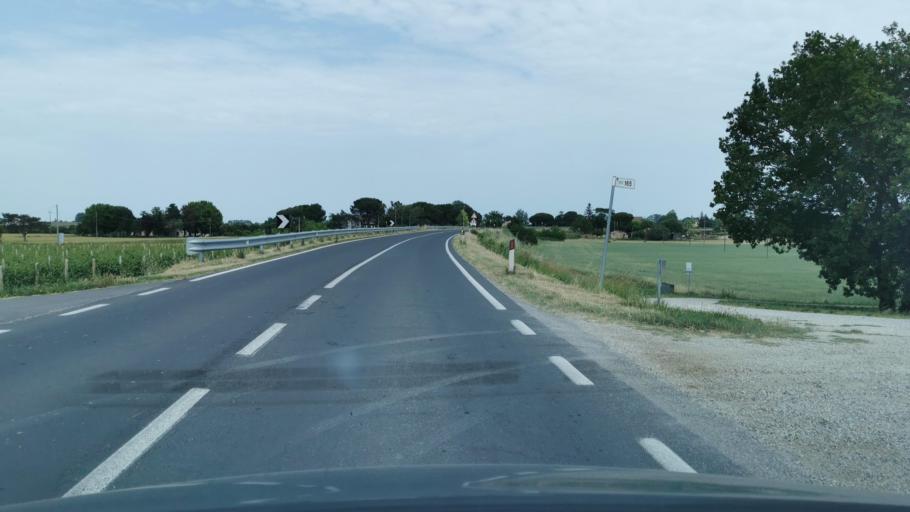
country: IT
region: Emilia-Romagna
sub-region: Provincia di Ravenna
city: Sant'Alberto
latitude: 44.5376
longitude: 12.1295
